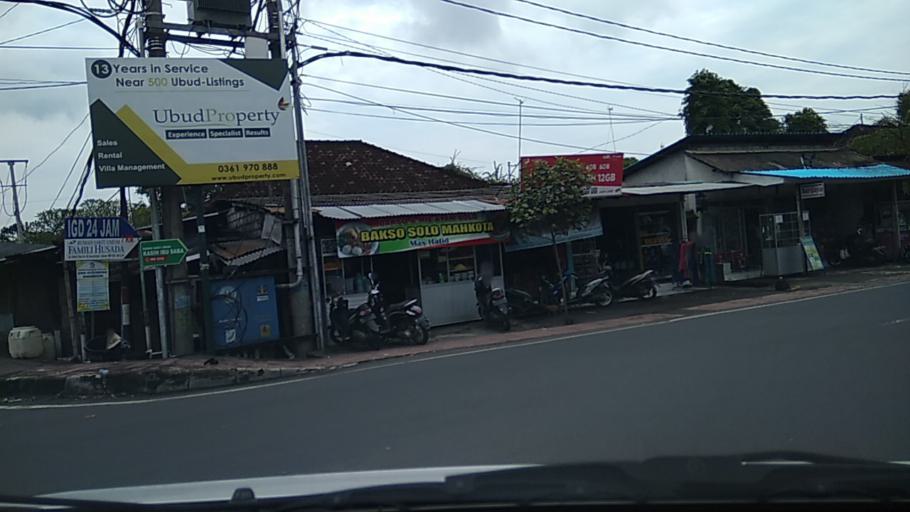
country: ID
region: Bali
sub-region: Kabupaten Gianyar
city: Ubud
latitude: -8.5238
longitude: 115.2921
